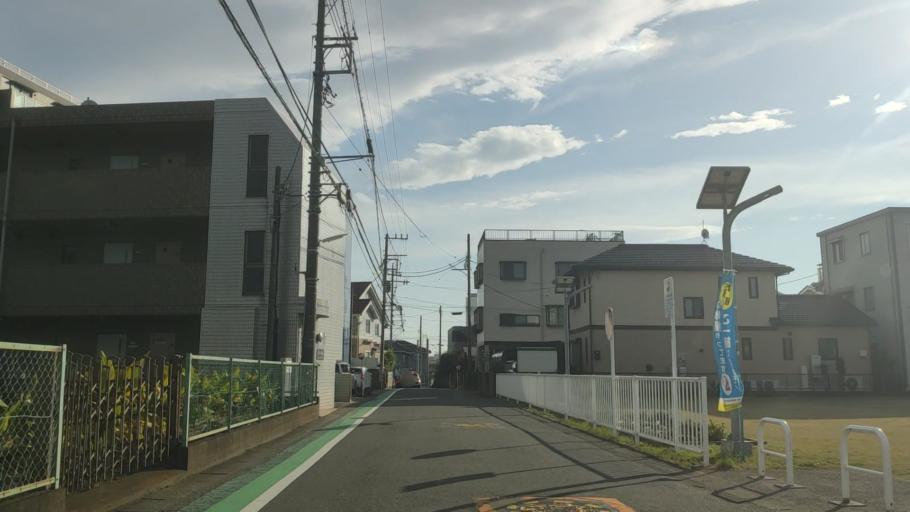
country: JP
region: Kanagawa
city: Zama
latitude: 35.4582
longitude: 139.3947
